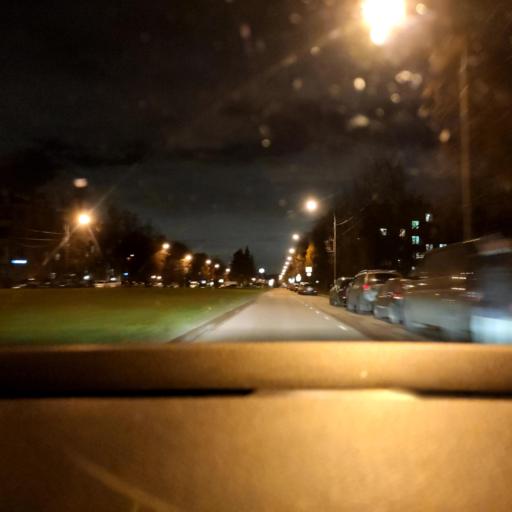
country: RU
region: Moscow
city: Vostochnyy
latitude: 55.8201
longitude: 37.8699
